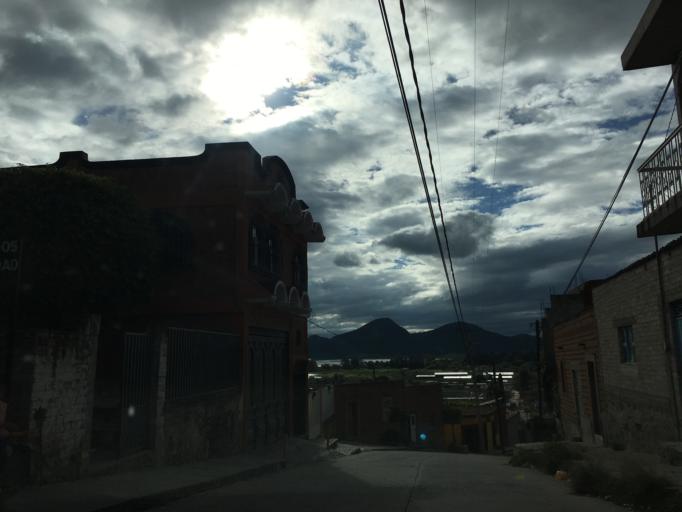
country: MX
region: Guanajuato
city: Iramuco
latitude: 19.9578
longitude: -100.9323
